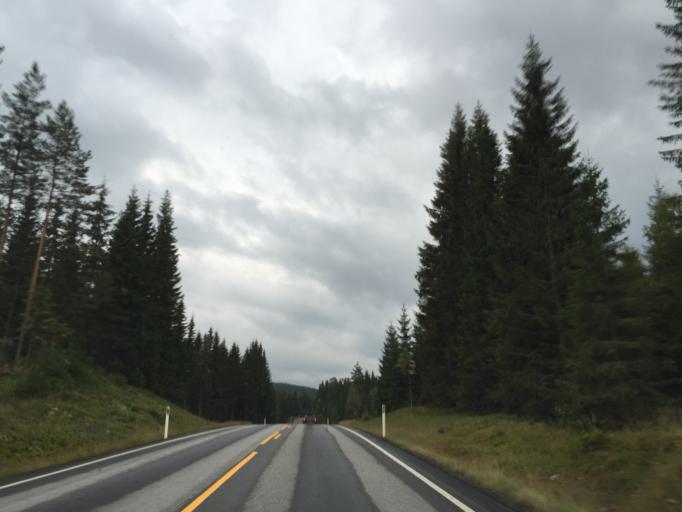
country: NO
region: Hedmark
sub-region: Nord-Odal
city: Sand
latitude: 60.5095
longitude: 11.5085
